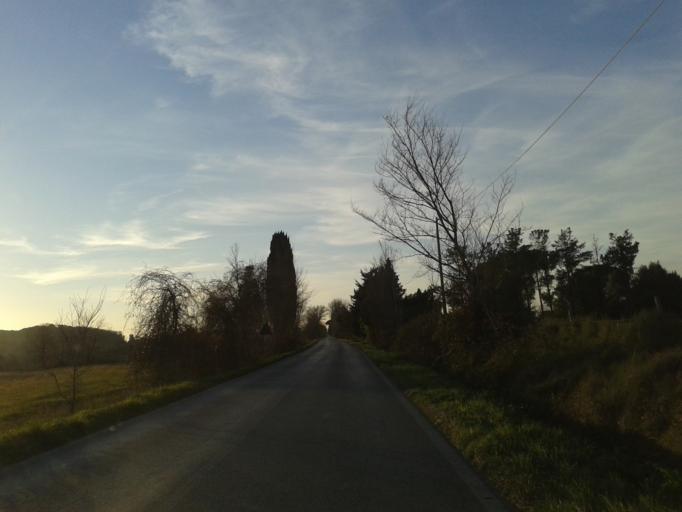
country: IT
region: Tuscany
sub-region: Provincia di Livorno
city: Guasticce
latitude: 43.5974
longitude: 10.4302
